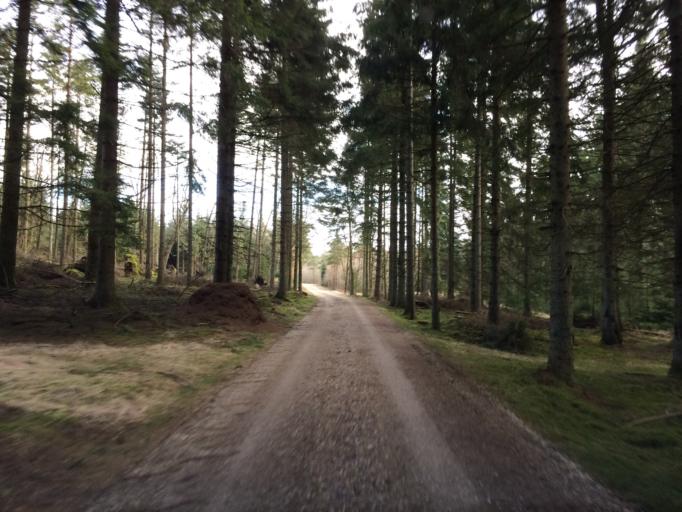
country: DK
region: Central Jutland
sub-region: Holstebro Kommune
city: Ulfborg
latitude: 56.2645
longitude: 8.4449
